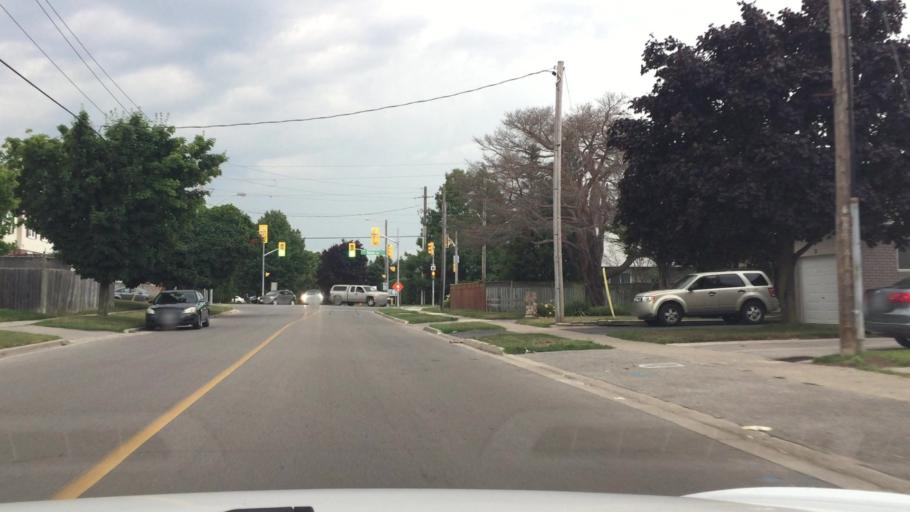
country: CA
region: Ontario
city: Oshawa
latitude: 43.9101
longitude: -78.8042
